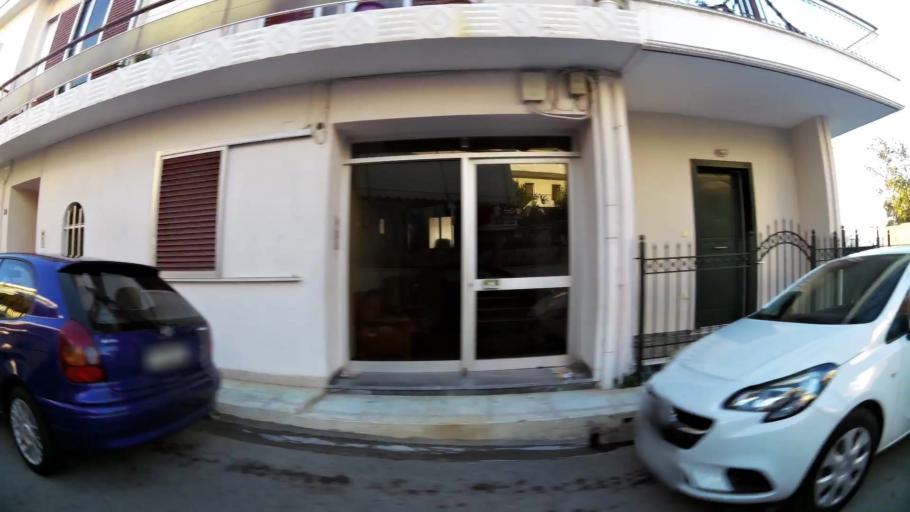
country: GR
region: Attica
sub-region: Nomarchia Anatolikis Attikis
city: Spata
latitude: 37.9663
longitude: 23.9096
